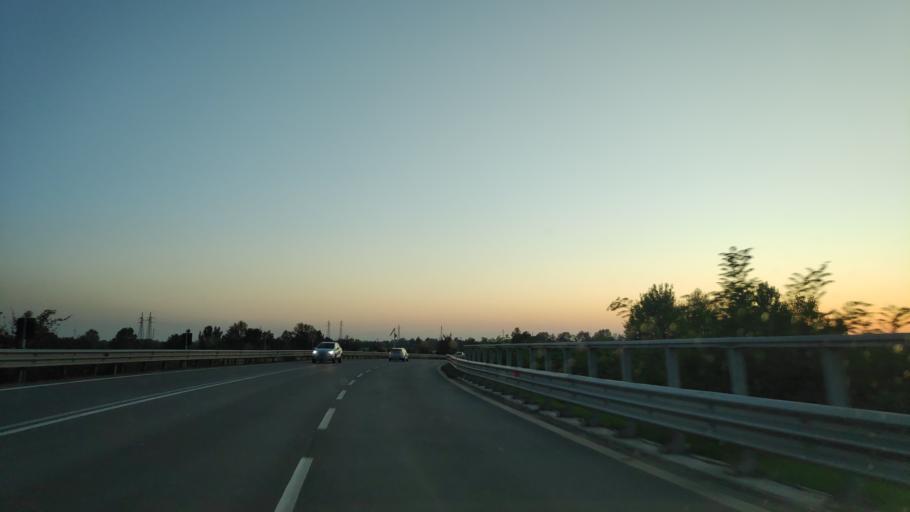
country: IT
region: Lombardy
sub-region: Citta metropolitana di Milano
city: Gaggiano
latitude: 45.4076
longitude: 9.0260
